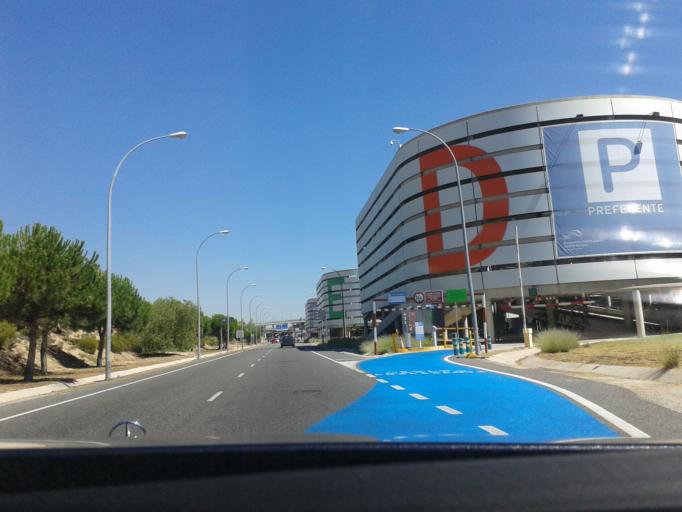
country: ES
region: Madrid
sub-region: Provincia de Madrid
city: Barajas de Madrid
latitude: 40.4914
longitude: -3.5954
